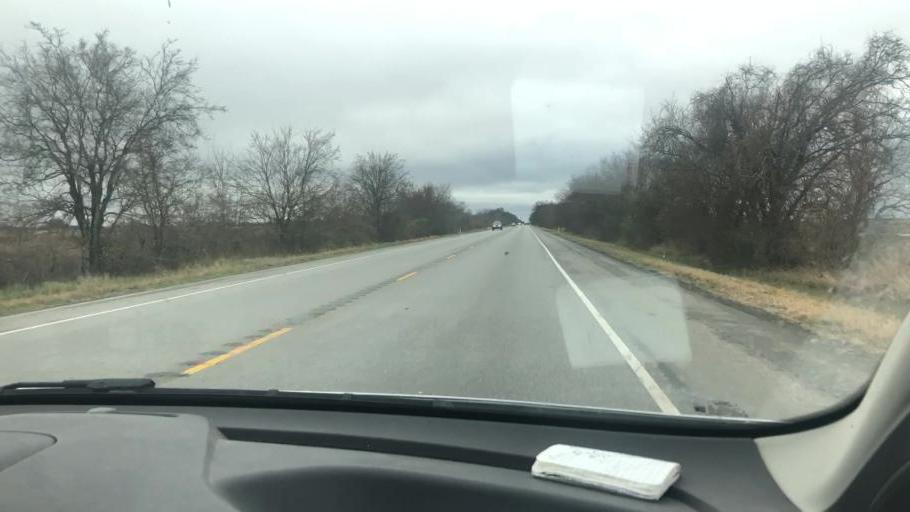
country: US
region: Texas
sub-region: Matagorda County
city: Bay City
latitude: 29.1148
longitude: -95.9798
